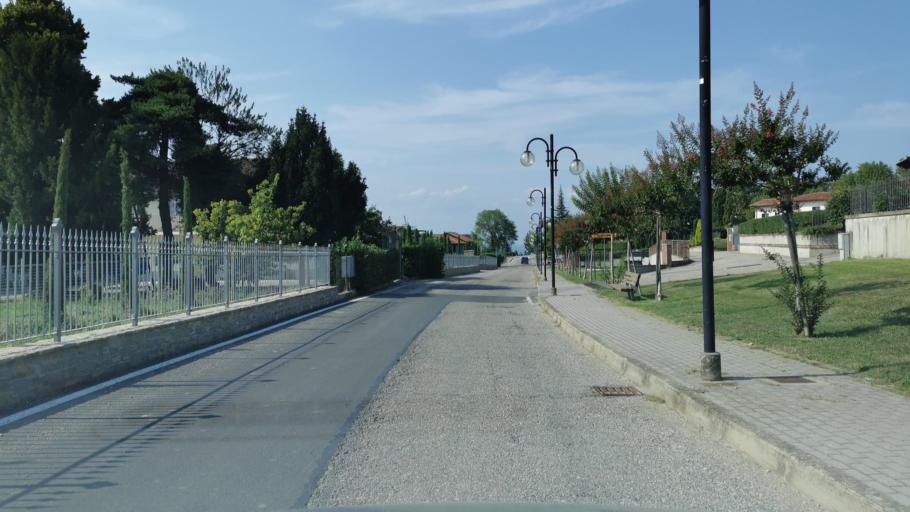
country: IT
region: Piedmont
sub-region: Provincia di Cuneo
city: La Morra
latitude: 44.6422
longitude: 7.9300
